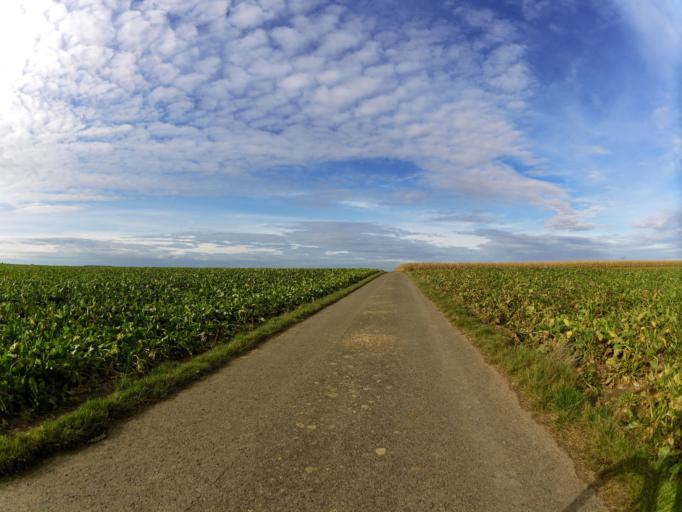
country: DE
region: Bavaria
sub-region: Regierungsbezirk Unterfranken
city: Giebelstadt
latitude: 49.6621
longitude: 9.9773
